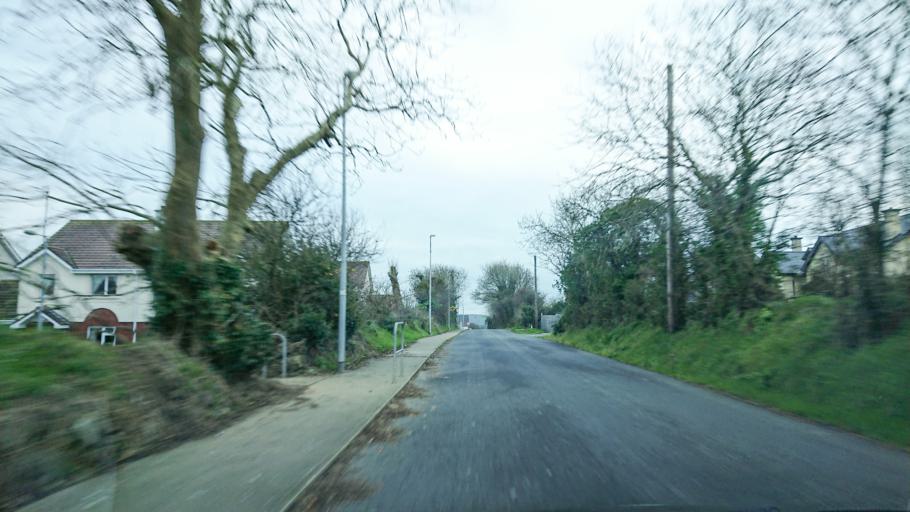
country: IE
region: Munster
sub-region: Waterford
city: Dunmore East
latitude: 52.2310
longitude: -6.9780
